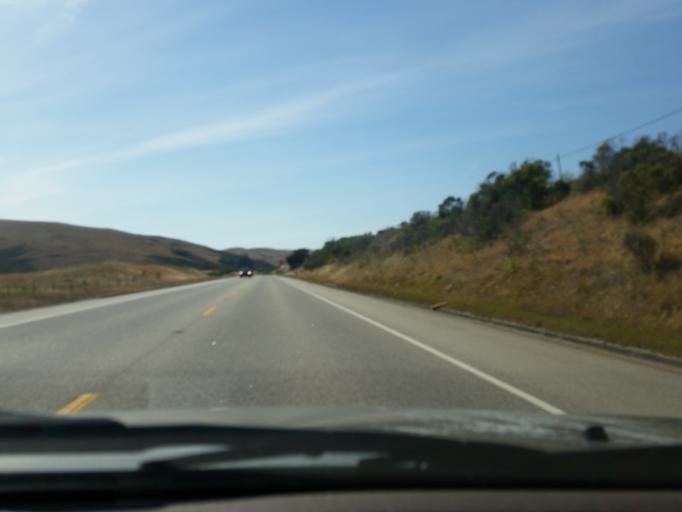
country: US
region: California
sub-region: San Luis Obispo County
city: Cayucos
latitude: 35.4621
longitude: -120.9667
